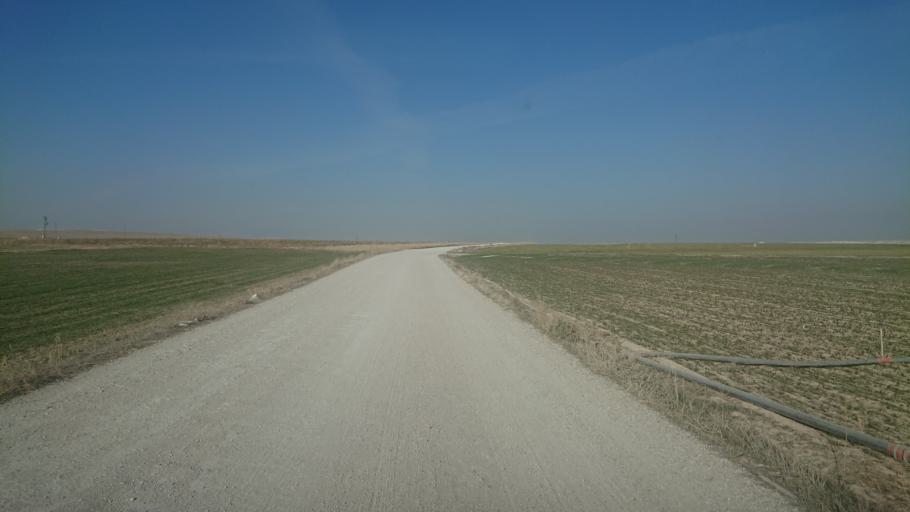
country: TR
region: Aksaray
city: Sultanhani
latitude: 38.0410
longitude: 33.6058
